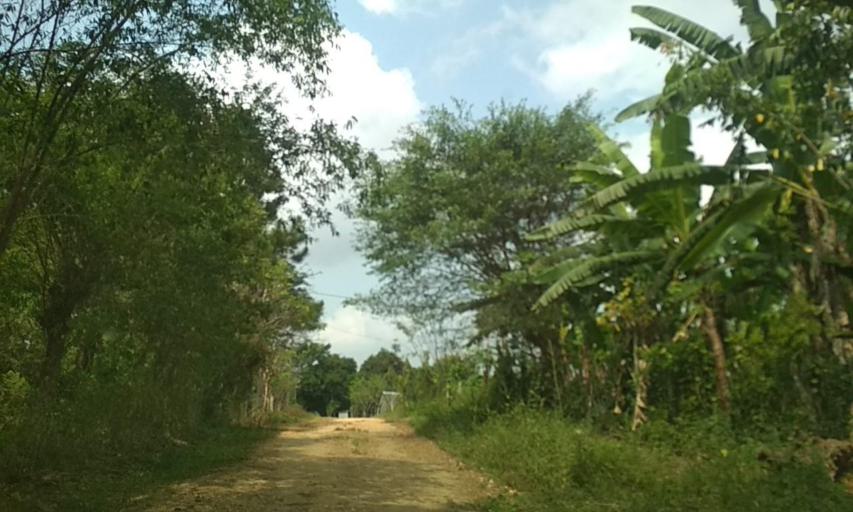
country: MX
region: Tabasco
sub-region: Huimanguillo
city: Francisco Rueda
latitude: 17.6552
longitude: -93.7522
